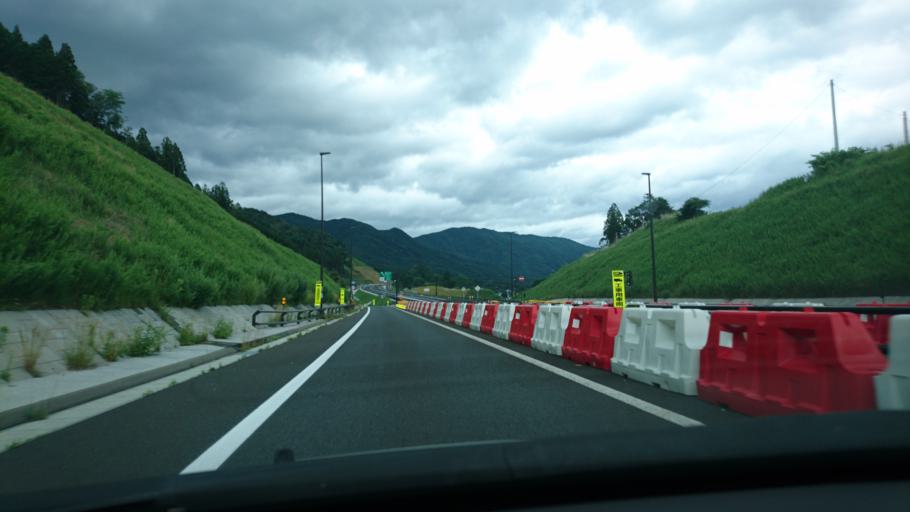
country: JP
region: Iwate
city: Ofunato
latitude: 39.1474
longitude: 141.8266
